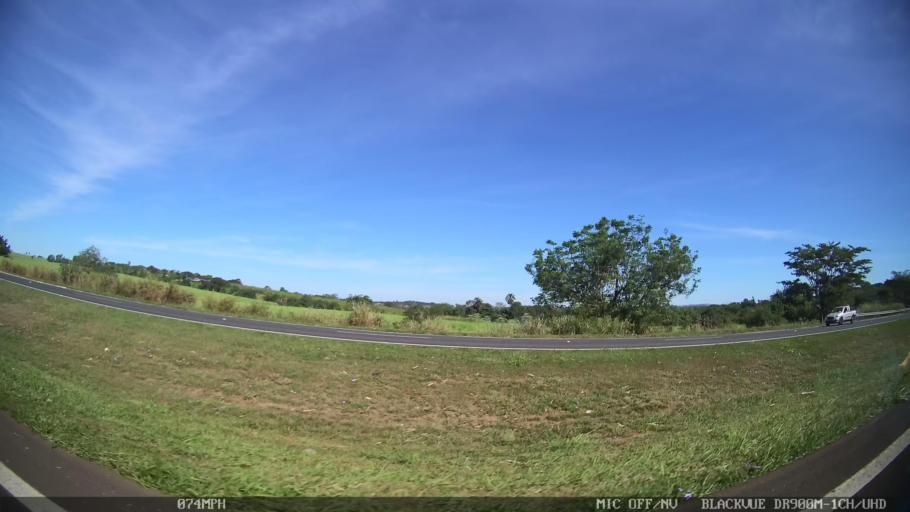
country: BR
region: Sao Paulo
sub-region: Porto Ferreira
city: Porto Ferreira
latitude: -21.7919
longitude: -47.5180
